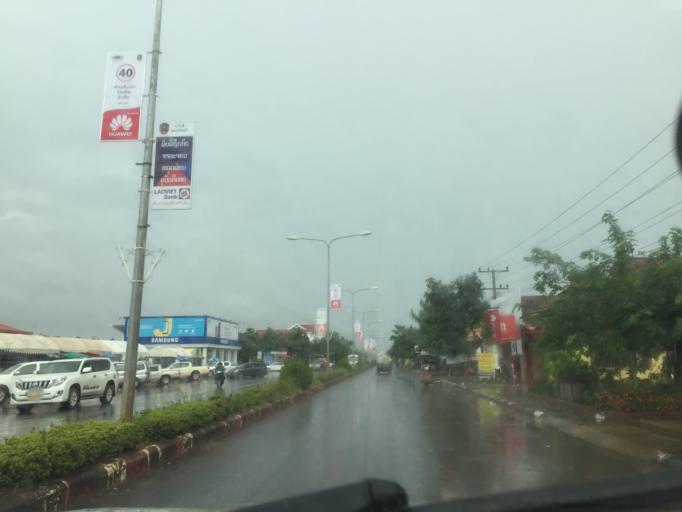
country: LA
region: Attapu
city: Attapu
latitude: 14.8165
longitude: 106.8185
